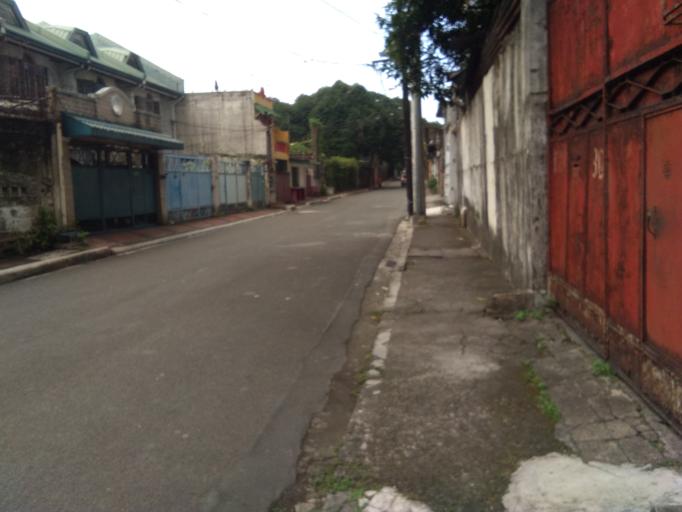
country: PH
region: Metro Manila
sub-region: San Juan
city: San Juan
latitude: 14.6194
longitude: 121.0424
